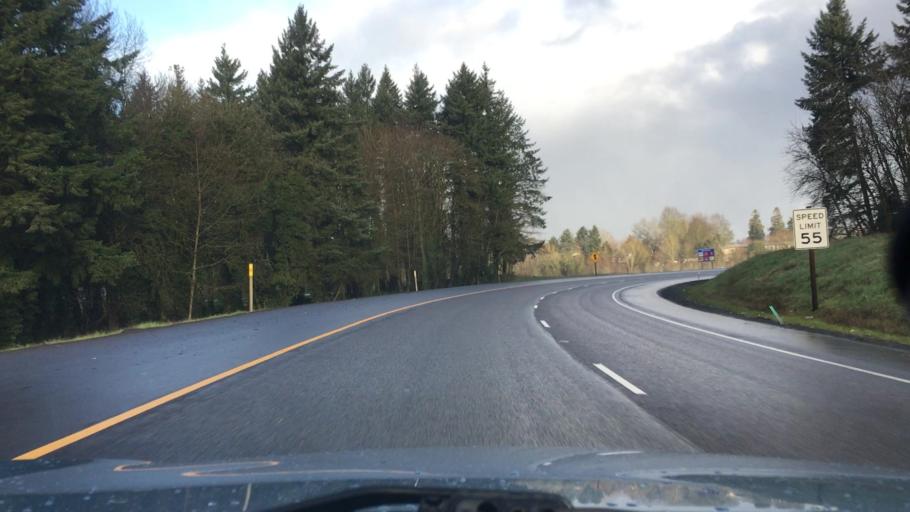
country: US
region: Oregon
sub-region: Washington County
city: Tualatin
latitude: 45.3709
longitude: -122.7547
